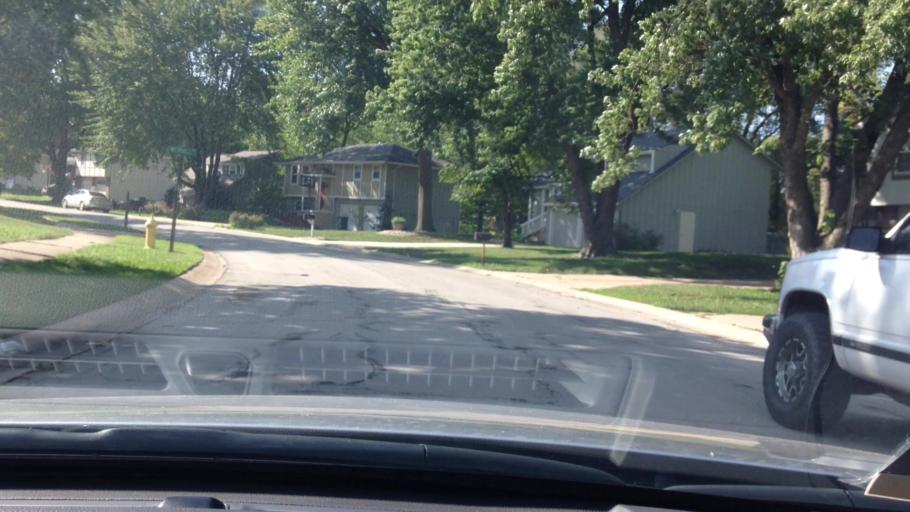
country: US
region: Missouri
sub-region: Jackson County
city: Grandview
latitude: 38.8826
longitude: -94.5042
